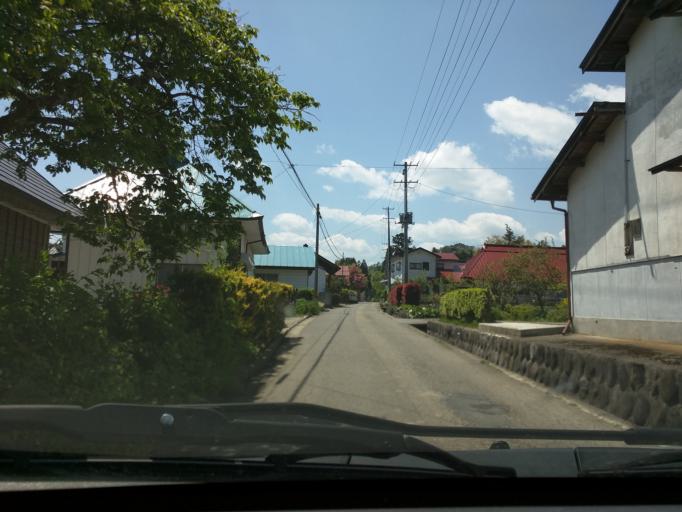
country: JP
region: Fukushima
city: Kitakata
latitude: 37.6379
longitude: 139.8364
